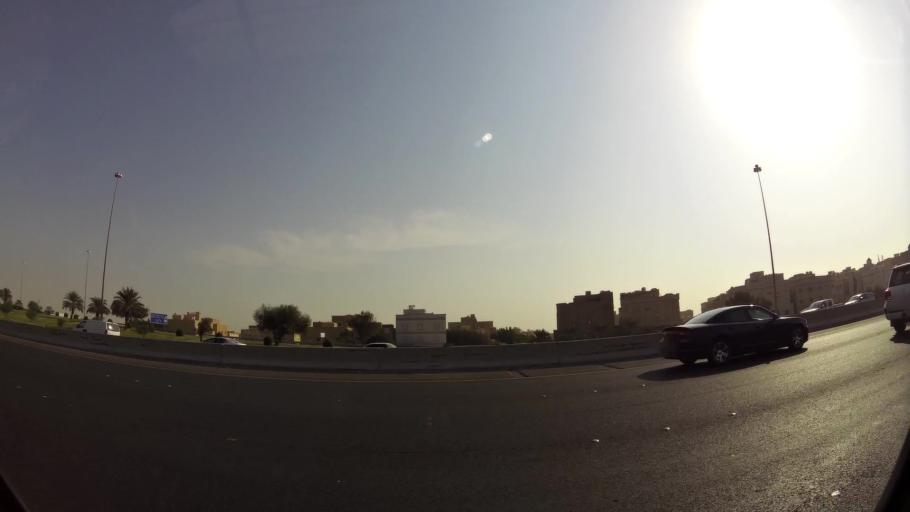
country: KW
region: Al Ahmadi
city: Ar Riqqah
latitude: 29.1286
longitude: 48.0919
